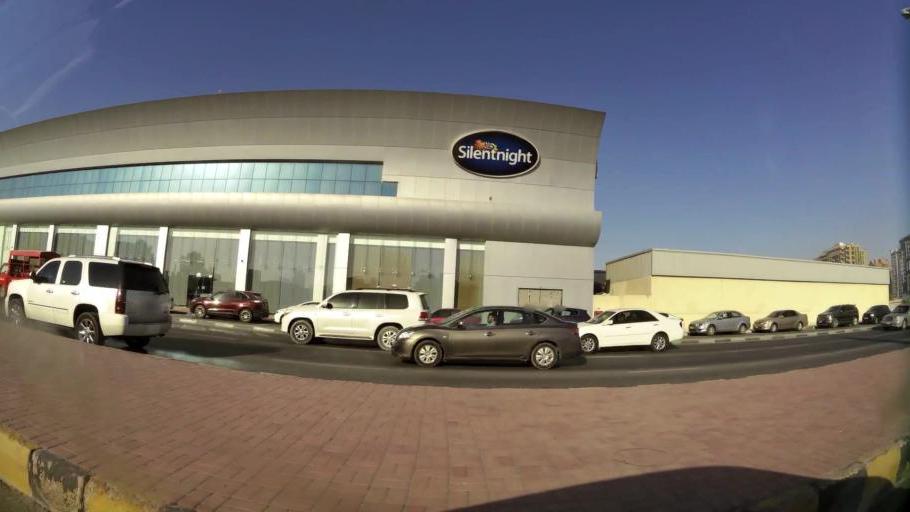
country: AE
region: Ajman
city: Ajman
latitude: 25.3919
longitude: 55.4553
